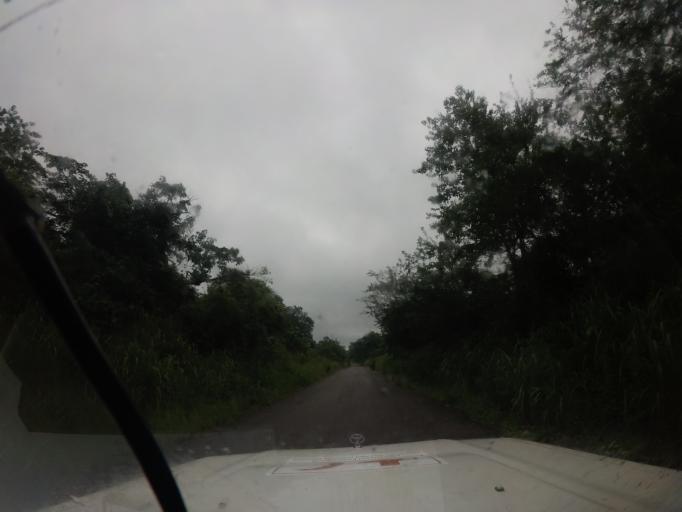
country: SL
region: Northern Province
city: Kabala
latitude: 9.4483
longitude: -11.7060
